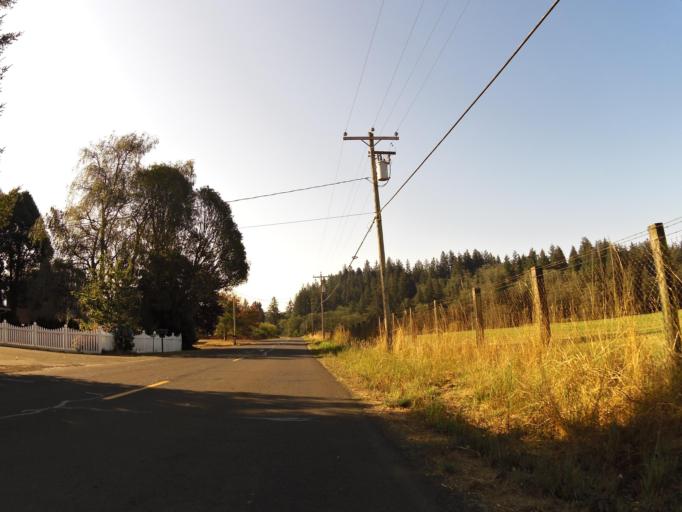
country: US
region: Oregon
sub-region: Tillamook County
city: Tillamook
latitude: 45.4234
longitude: -123.7828
